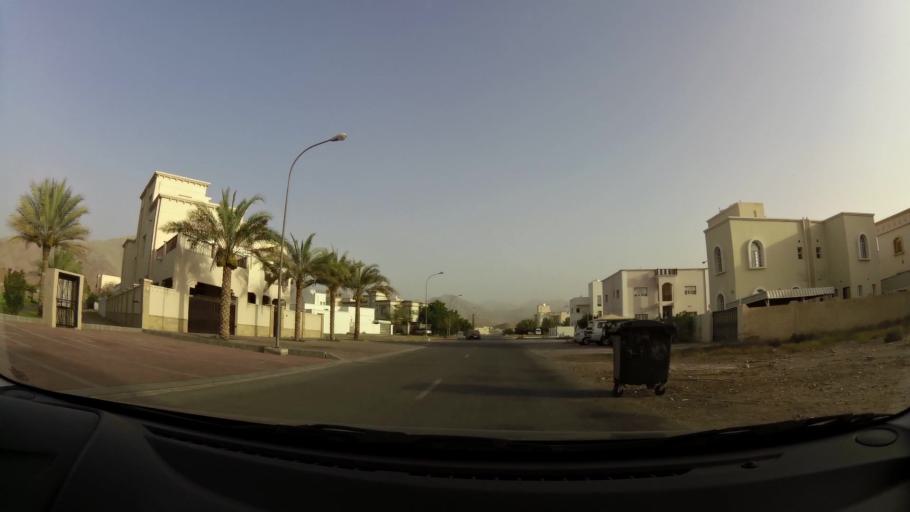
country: OM
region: Muhafazat Masqat
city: Bawshar
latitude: 23.5333
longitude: 58.3527
